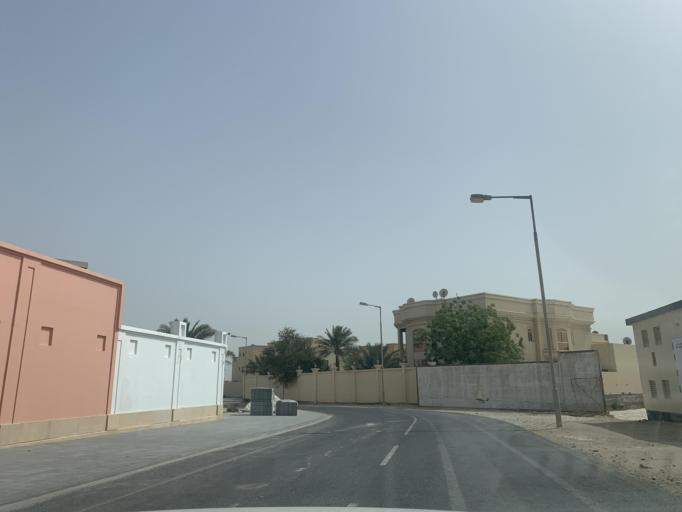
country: BH
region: Central Governorate
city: Madinat Hamad
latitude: 26.1449
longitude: 50.5132
